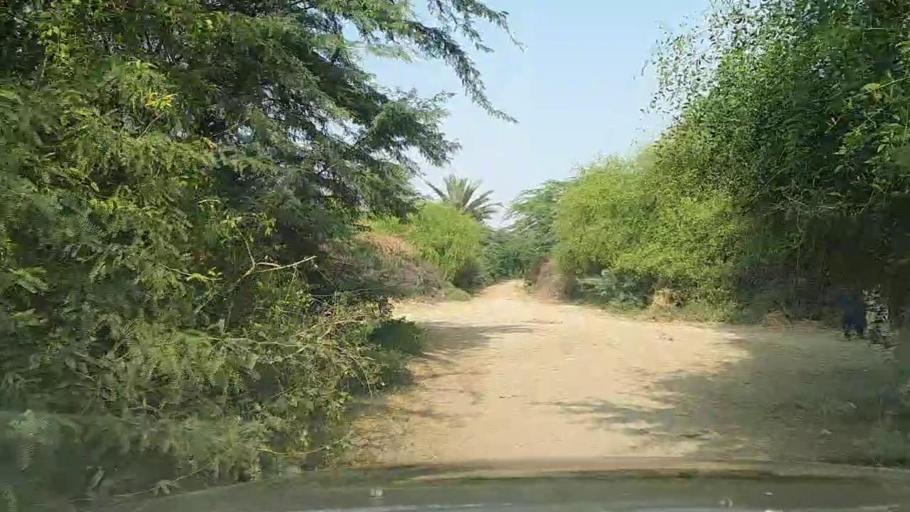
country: PK
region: Sindh
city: Mirpur Batoro
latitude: 24.6817
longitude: 68.2366
